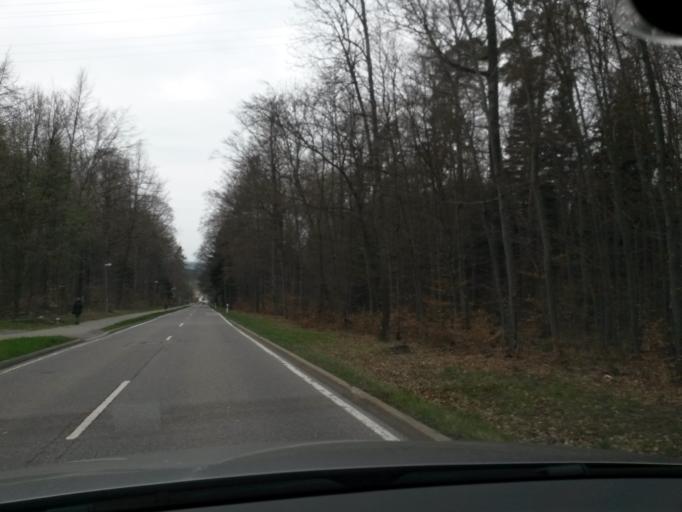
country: DE
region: Baden-Wuerttemberg
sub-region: Karlsruhe Region
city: Neuenburg
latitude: 48.8548
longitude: 8.5812
